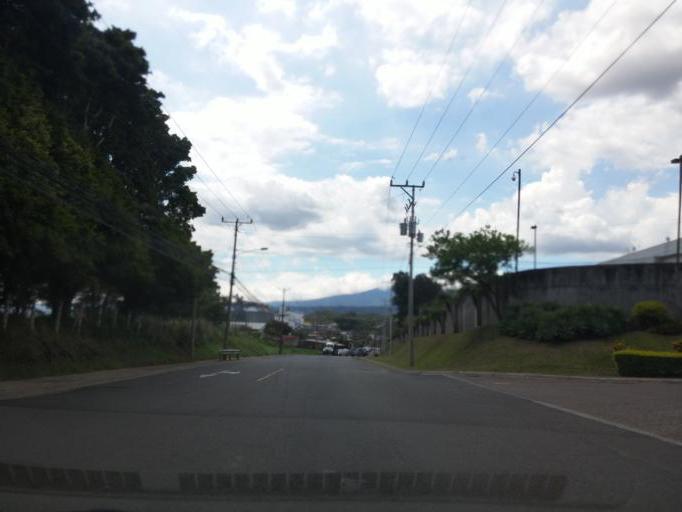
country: CR
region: Heredia
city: Llorente
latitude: 10.0003
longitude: -84.1698
